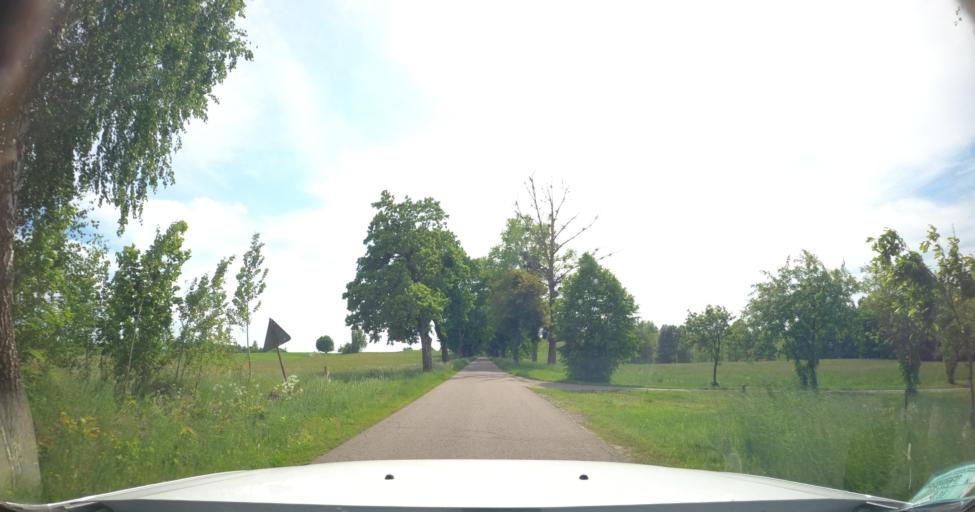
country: PL
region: Warmian-Masurian Voivodeship
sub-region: Powiat lidzbarski
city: Lubomino
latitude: 54.0938
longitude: 20.3073
